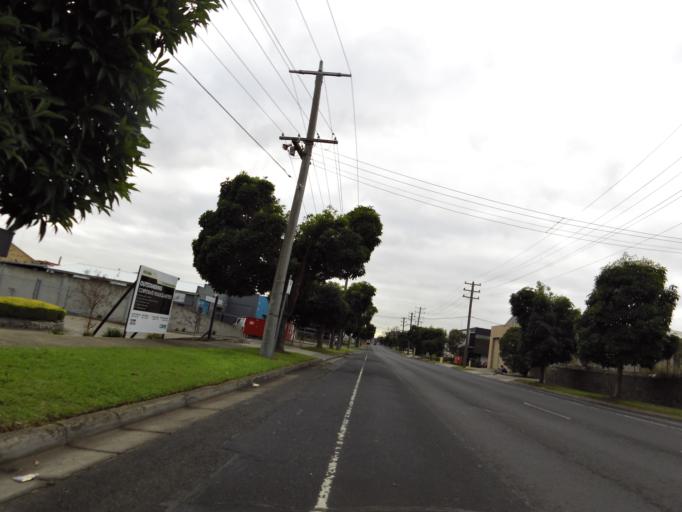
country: AU
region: Victoria
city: Heidelberg West
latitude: -37.7539
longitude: 145.0287
